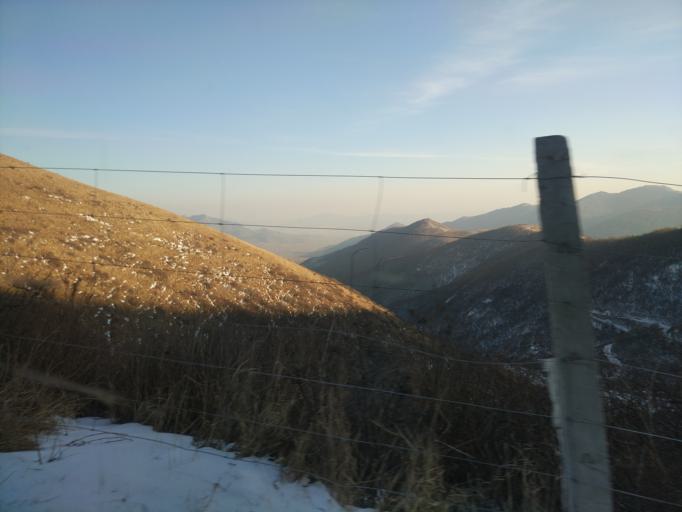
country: CN
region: Hebei
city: Xiwanzi
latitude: 40.8745
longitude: 115.4531
